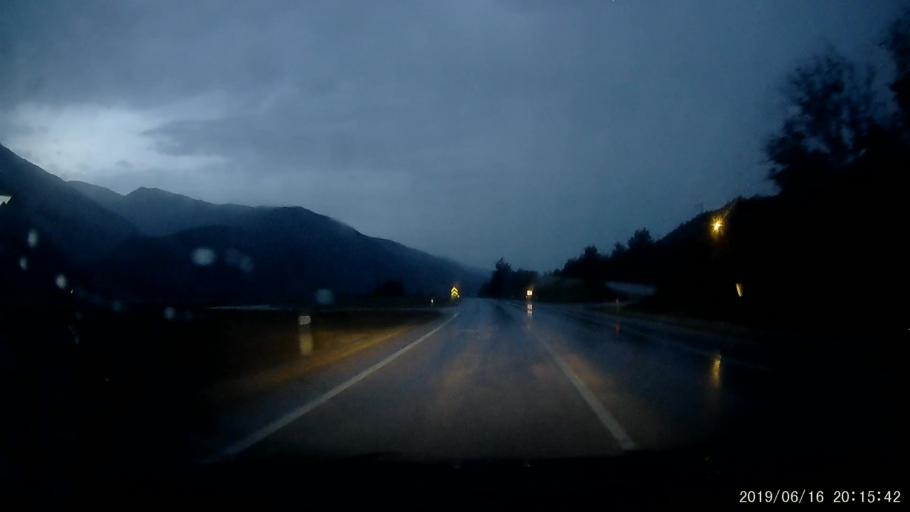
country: TR
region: Tokat
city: Resadiye
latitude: 40.3558
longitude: 37.4577
